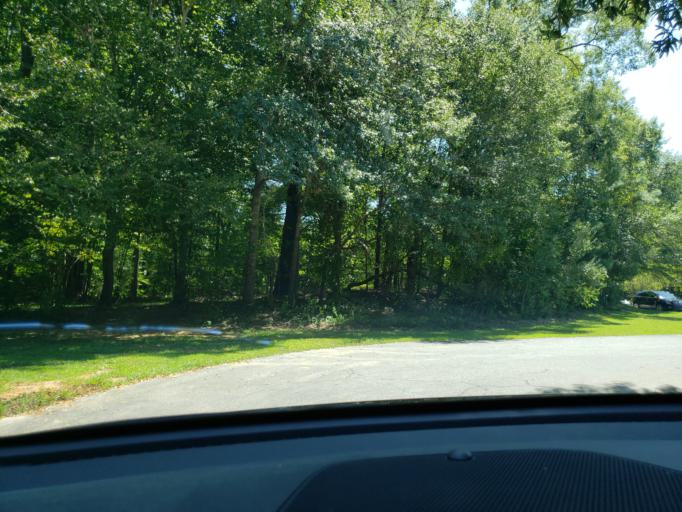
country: US
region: North Carolina
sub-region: Orange County
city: Chapel Hill
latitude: 35.9438
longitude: -78.9793
